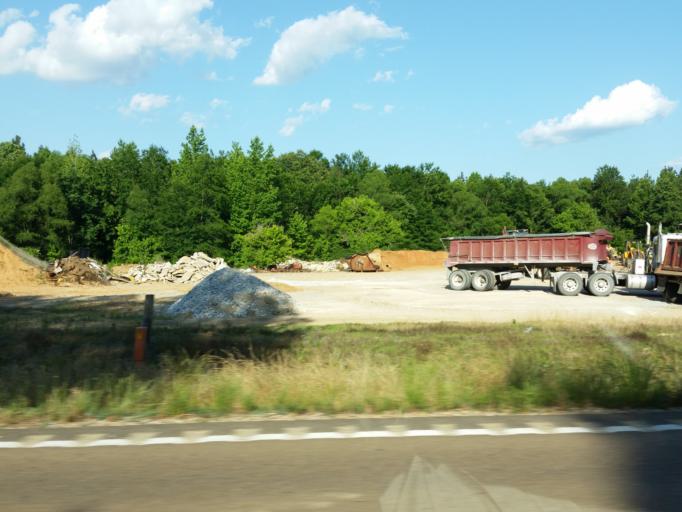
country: US
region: Mississippi
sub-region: Calhoun County
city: Calhoun City
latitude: 33.7697
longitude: -89.3639
